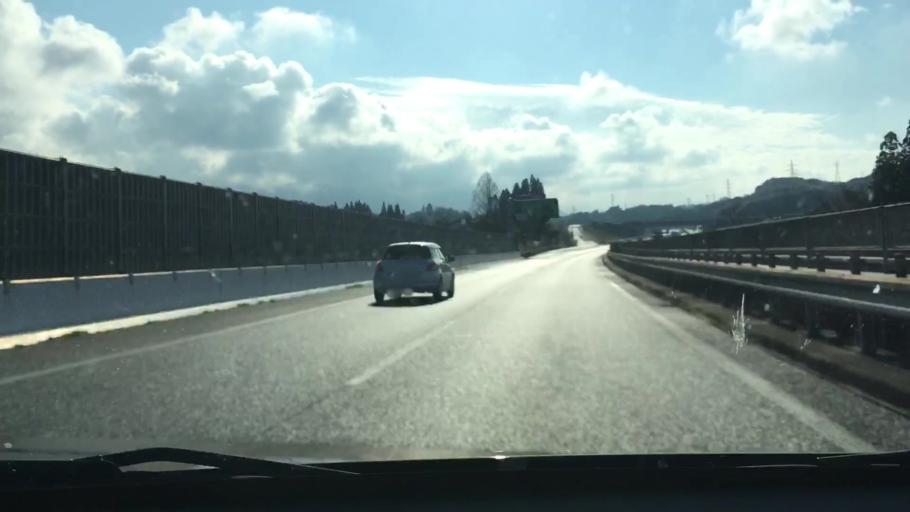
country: JP
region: Kumamoto
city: Matsubase
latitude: 32.5805
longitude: 130.7140
